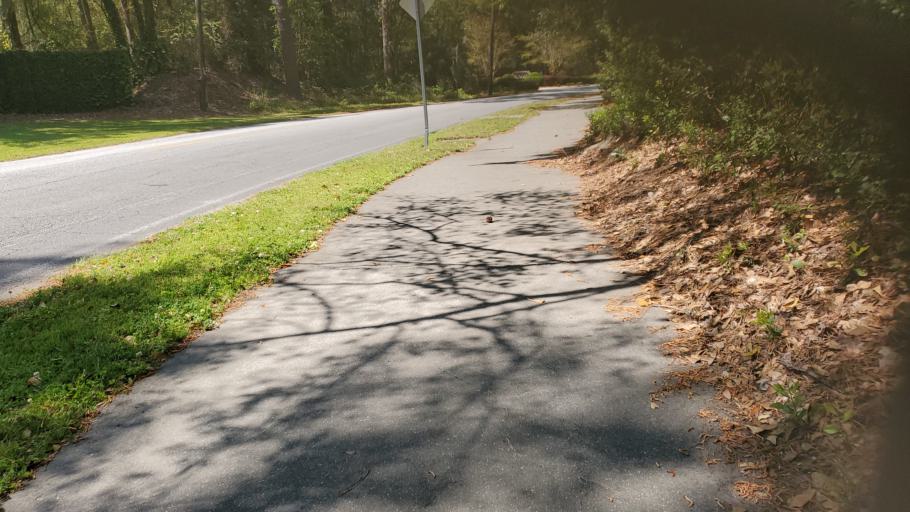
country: US
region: Georgia
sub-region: Chatham County
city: Wilmington Island
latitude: 32.0032
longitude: -80.9857
